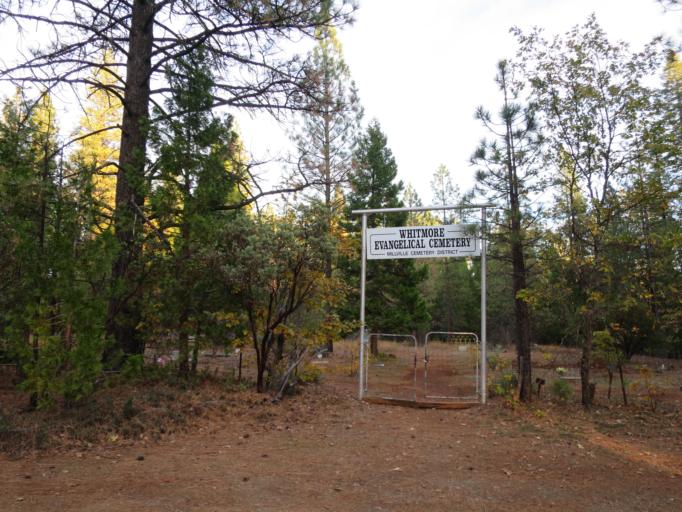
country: US
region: California
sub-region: Shasta County
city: Shingletown
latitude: 40.6233
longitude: -121.8570
